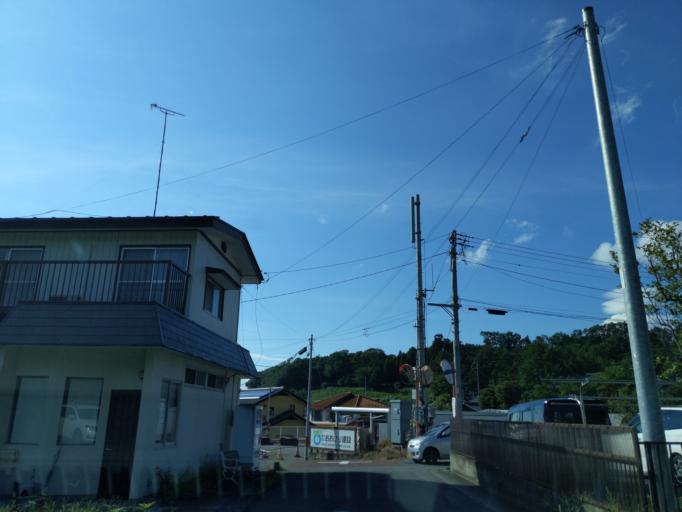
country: JP
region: Fukushima
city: Koriyama
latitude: 37.3963
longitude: 140.4240
